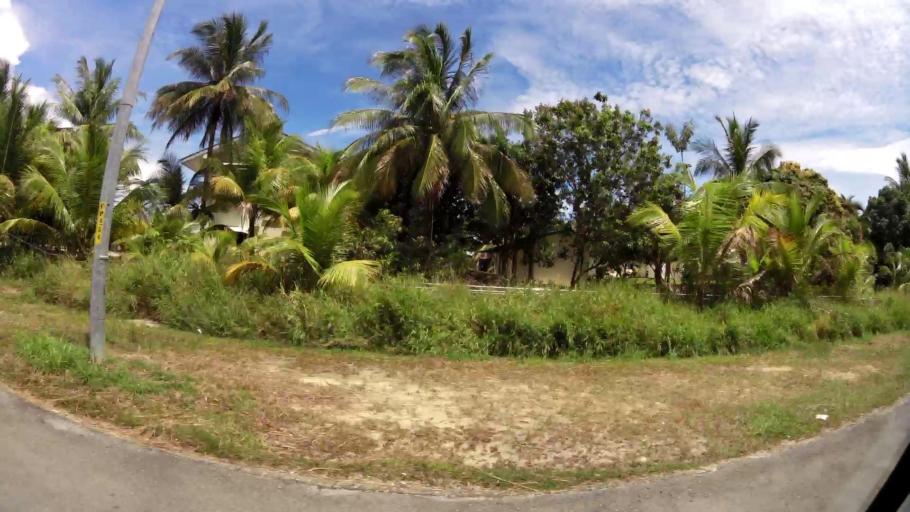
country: BN
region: Brunei and Muara
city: Bandar Seri Begawan
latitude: 4.9609
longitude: 114.9036
